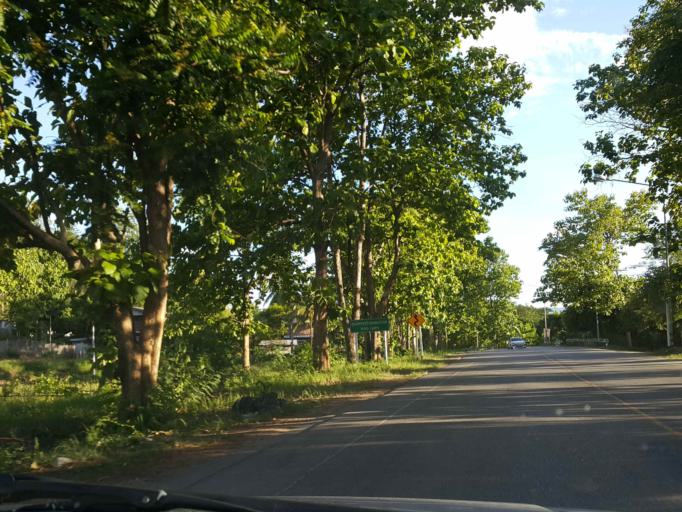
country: TH
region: Chiang Mai
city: Chom Thong
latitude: 18.4849
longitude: 98.6702
